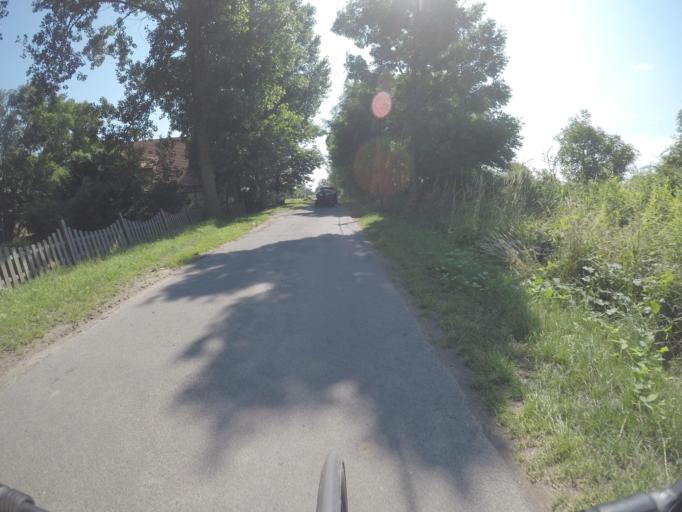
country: DE
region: Mecklenburg-Vorpommern
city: Rambin
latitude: 54.4347
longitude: 13.1733
